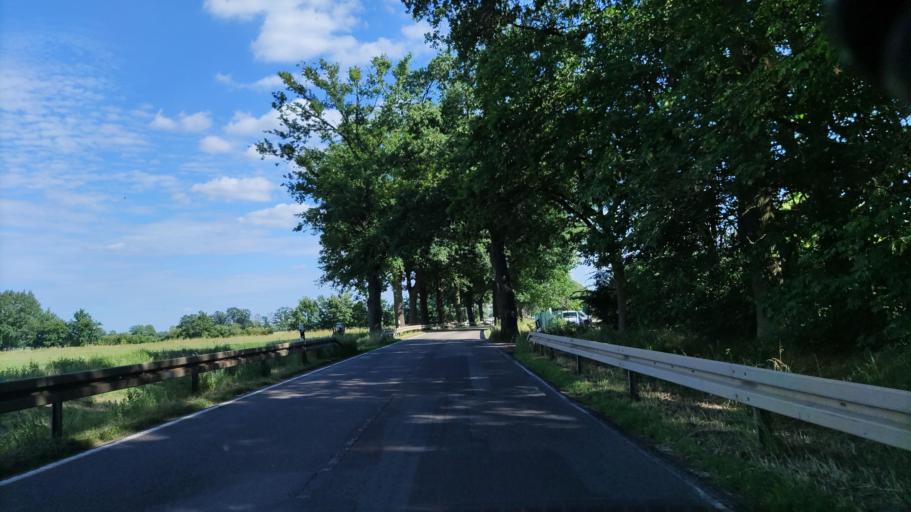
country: DE
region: Mecklenburg-Vorpommern
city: Domitz
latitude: 53.1654
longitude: 11.2394
